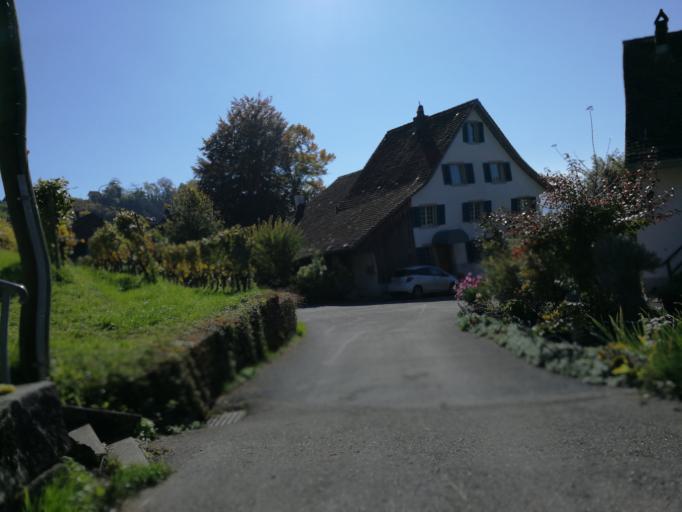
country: CH
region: Zurich
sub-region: Bezirk Meilen
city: Maennedorf / Ausserfeld
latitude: 47.2485
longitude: 8.7131
